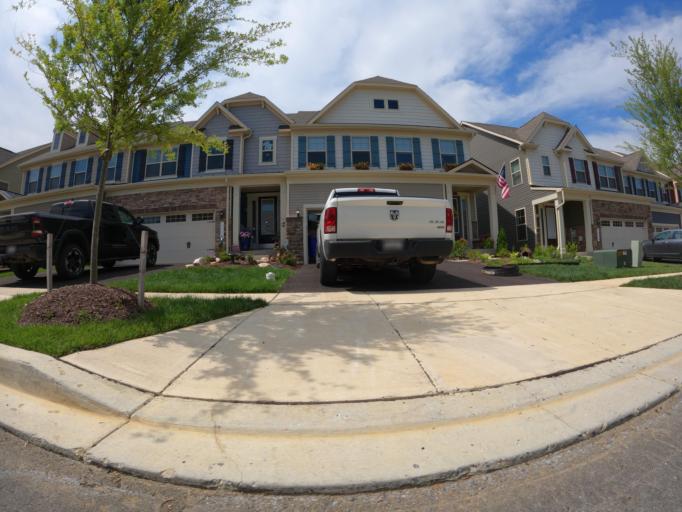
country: US
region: Maryland
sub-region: Frederick County
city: Brunswick
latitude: 39.3290
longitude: -77.6481
